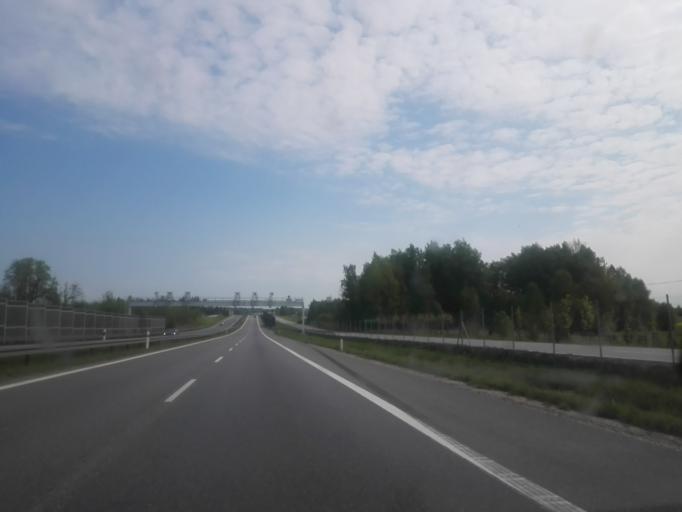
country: PL
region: Masovian Voivodeship
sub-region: Powiat zyrardowski
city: Radziejowice
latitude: 51.9885
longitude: 20.5396
